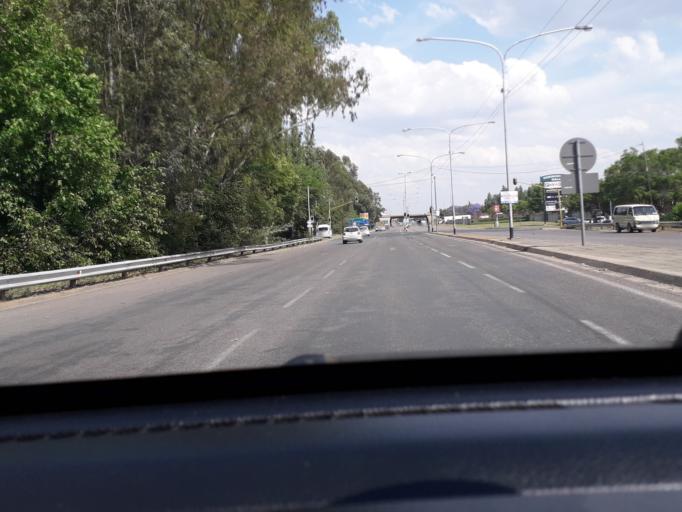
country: ZA
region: Gauteng
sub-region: City of Tshwane Metropolitan Municipality
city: Centurion
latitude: -25.8545
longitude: 28.2183
